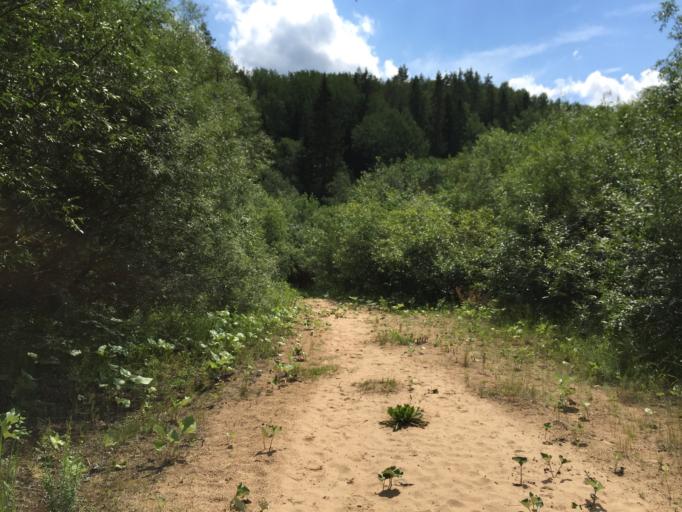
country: LV
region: Ligatne
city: Ligatne
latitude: 57.2546
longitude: 25.0621
